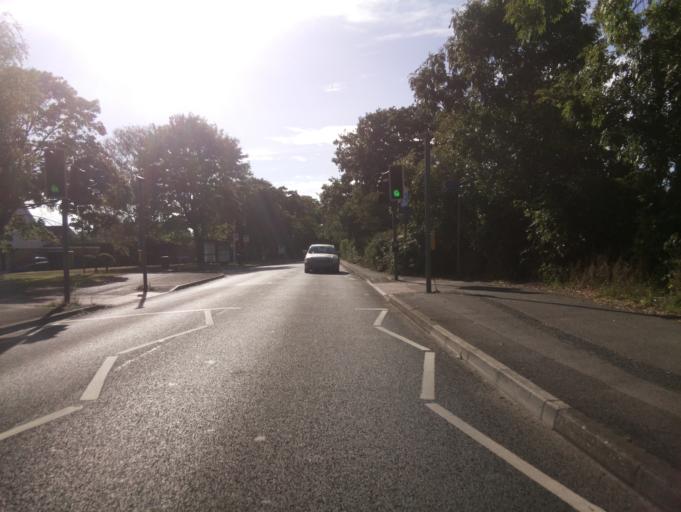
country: GB
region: England
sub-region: Hampshire
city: Romsey
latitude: 50.9860
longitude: -1.4654
